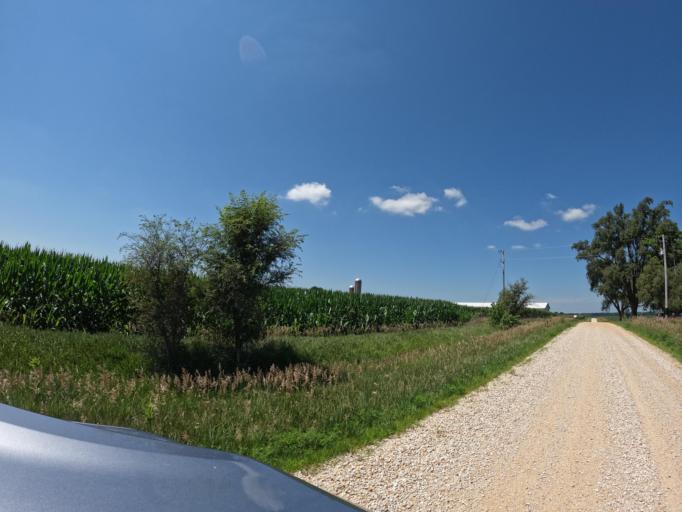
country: US
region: Iowa
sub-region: Clinton County
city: De Witt
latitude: 41.7793
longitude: -90.4030
